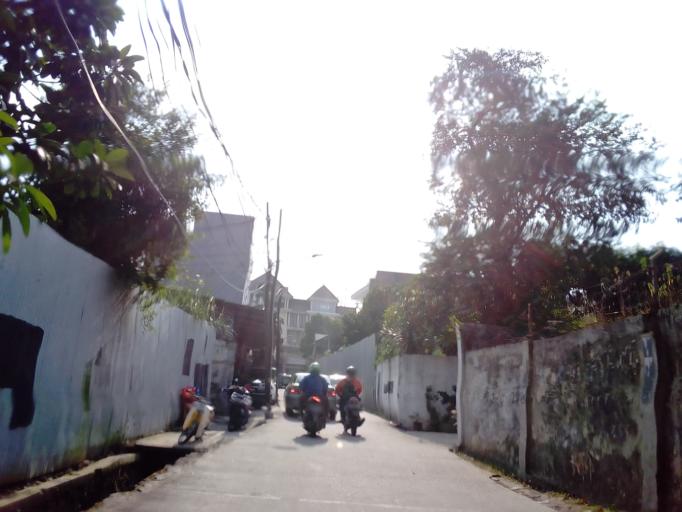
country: ID
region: Jakarta Raya
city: Jakarta
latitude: -6.2572
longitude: 106.7908
